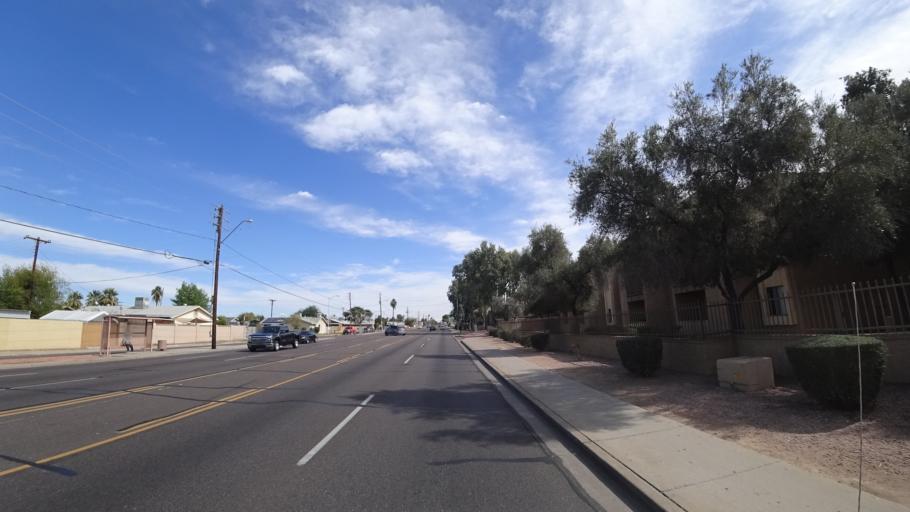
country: US
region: Arizona
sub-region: Maricopa County
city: Glendale
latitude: 33.4804
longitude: -112.1915
